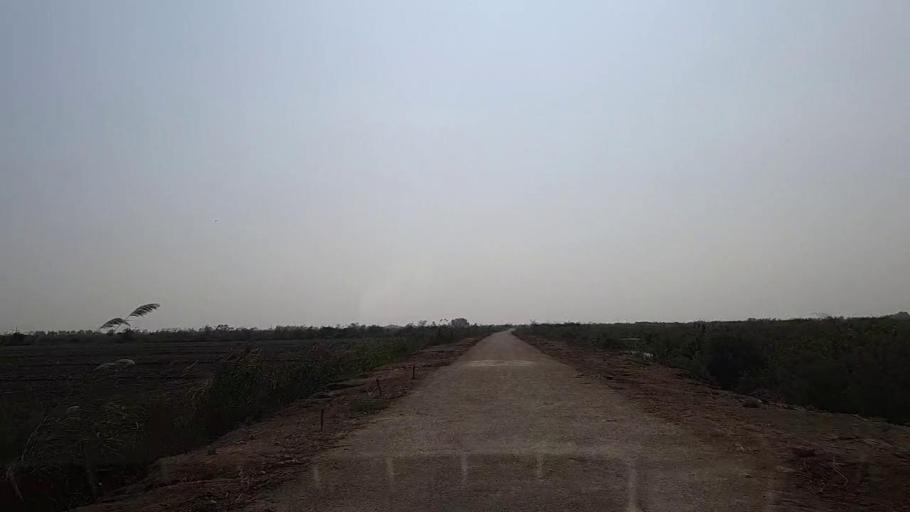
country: PK
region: Sindh
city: Mirpur Sakro
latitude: 24.6572
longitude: 67.6920
